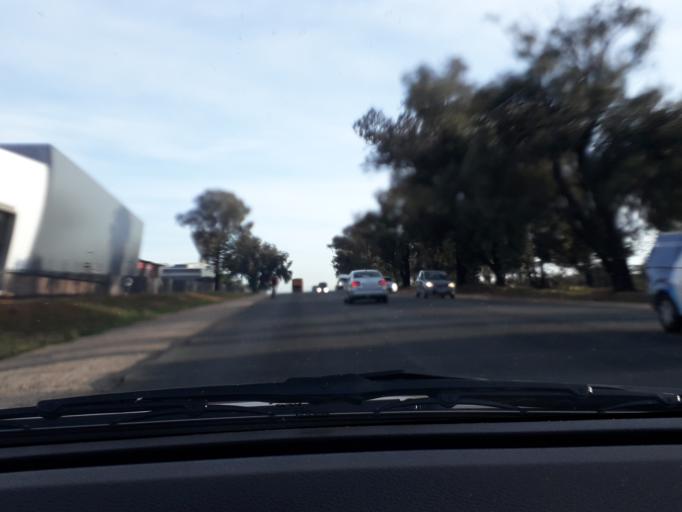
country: ZA
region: Gauteng
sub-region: City of Johannesburg Metropolitan Municipality
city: Midrand
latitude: -25.9422
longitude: 28.1444
